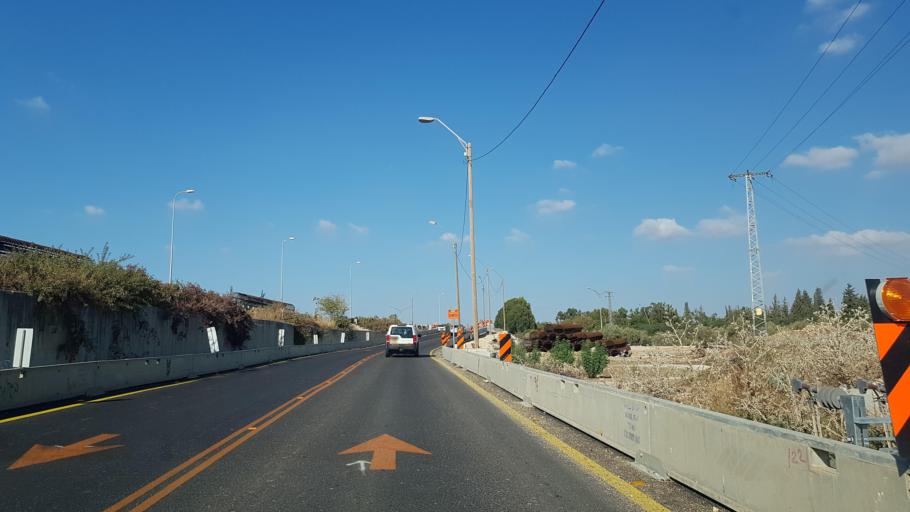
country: PS
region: West Bank
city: Tulkarm
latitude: 32.3352
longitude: 35.0073
